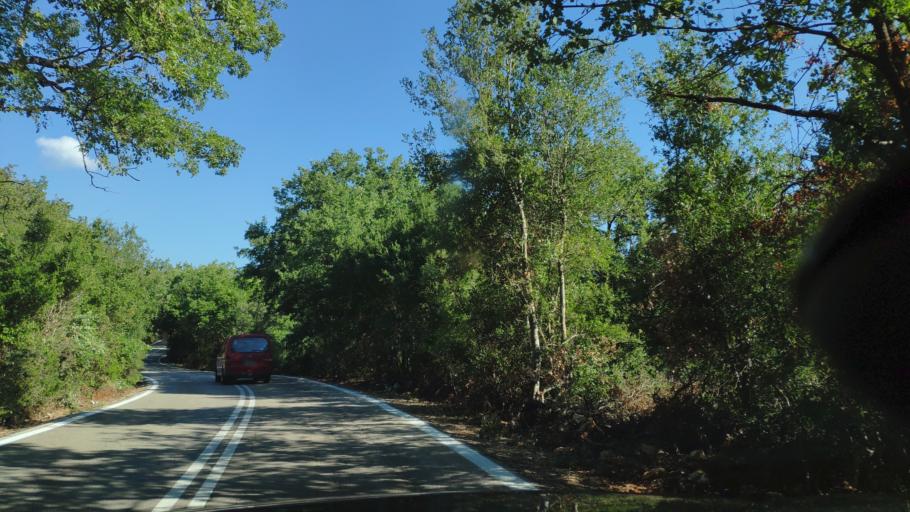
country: GR
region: West Greece
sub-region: Nomos Aitolias kai Akarnanias
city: Fitiai
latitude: 38.6905
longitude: 21.1138
